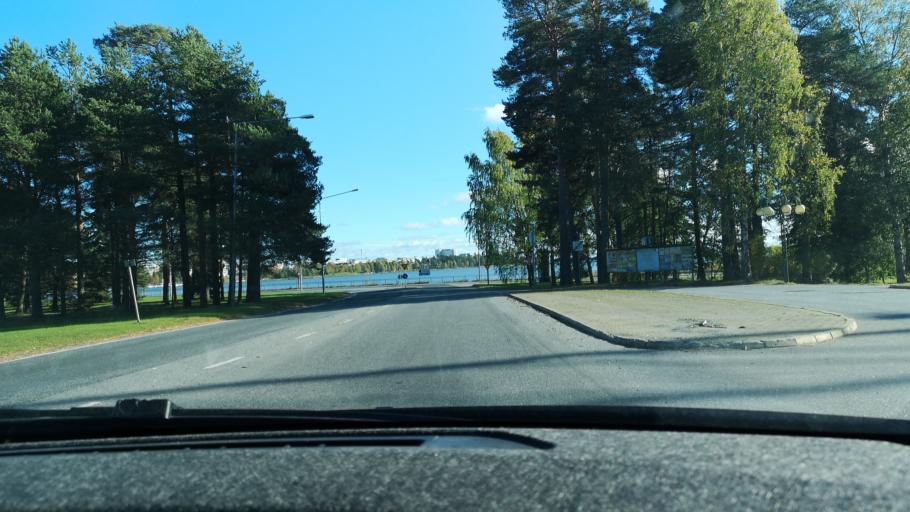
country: FI
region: Ostrobothnia
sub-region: Vaasa
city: Vaasa
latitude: 63.0919
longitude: 21.5883
